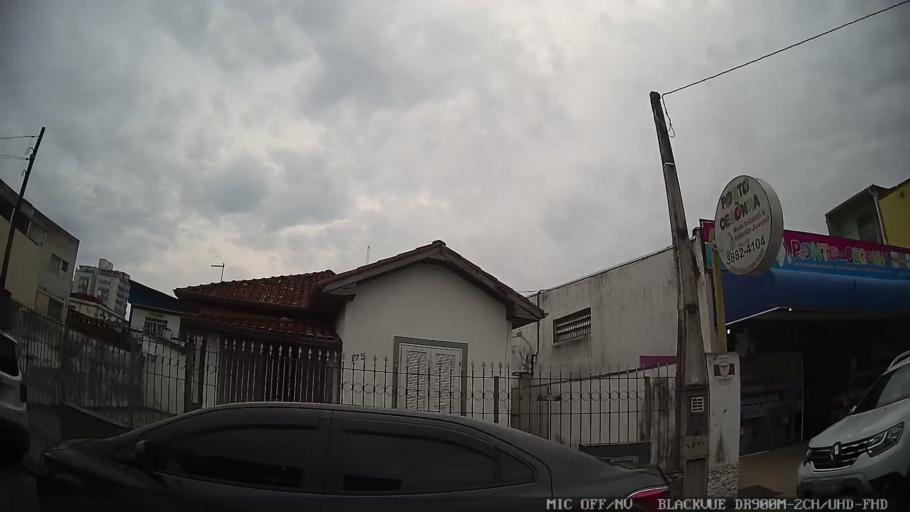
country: BR
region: Sao Paulo
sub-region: Caraguatatuba
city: Caraguatatuba
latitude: -23.6231
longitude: -45.4115
